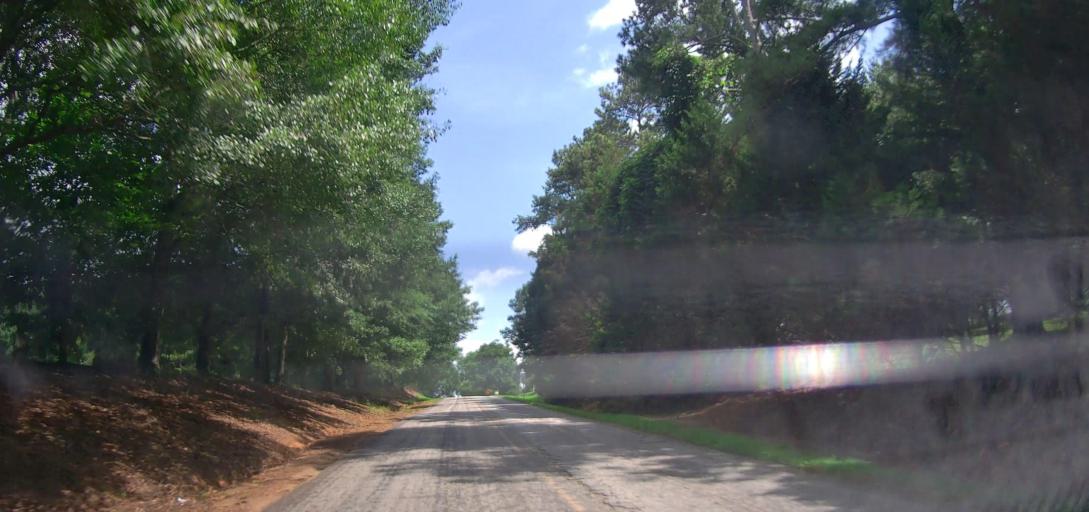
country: US
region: Georgia
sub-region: Carroll County
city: Bowdon
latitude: 33.5070
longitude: -85.3323
